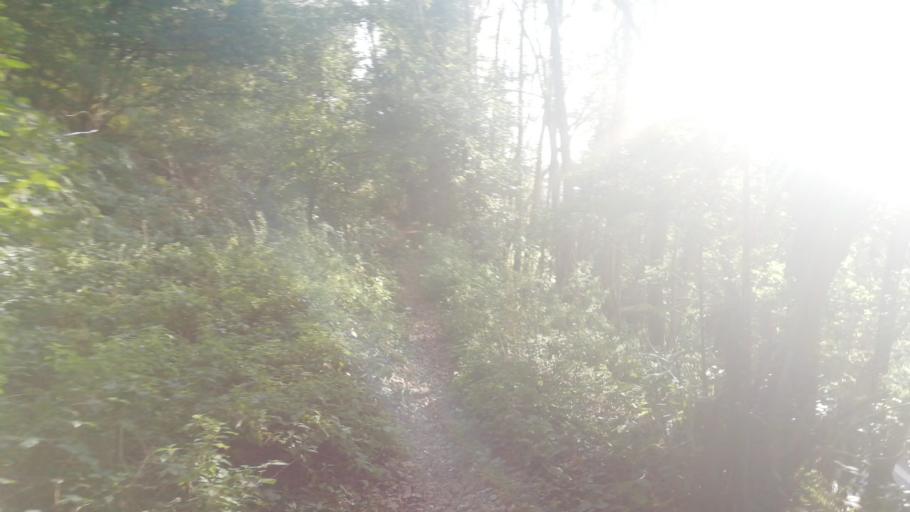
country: FR
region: Haute-Normandie
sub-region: Departement de la Seine-Maritime
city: Rolleville
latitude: 49.5897
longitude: 0.2121
